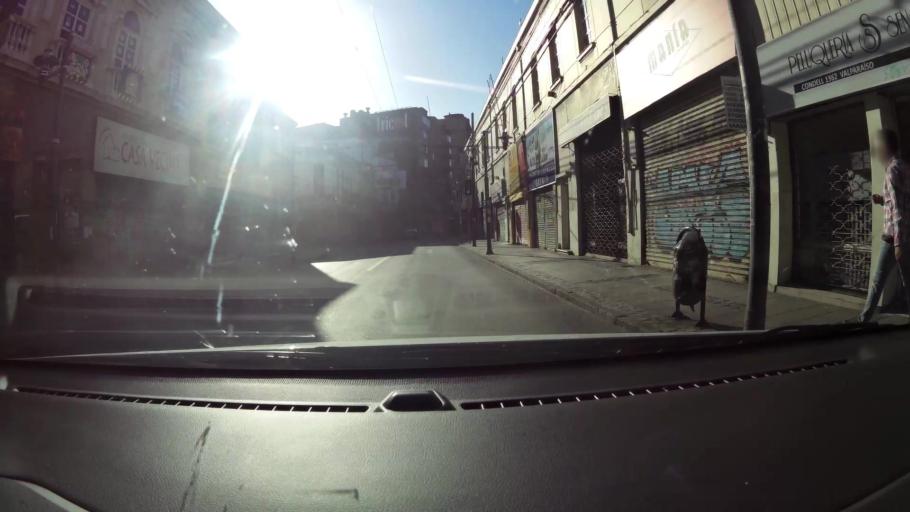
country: CL
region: Valparaiso
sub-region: Provincia de Valparaiso
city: Valparaiso
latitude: -33.0452
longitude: -71.6230
